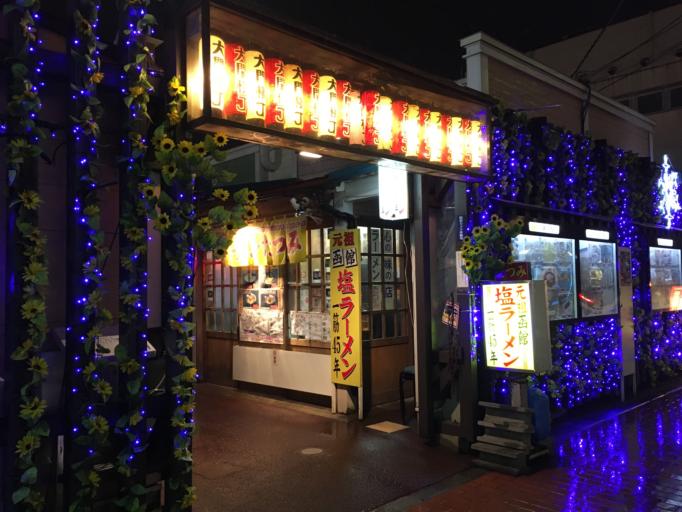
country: JP
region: Hokkaido
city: Hakodate
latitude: 41.7726
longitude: 140.7301
